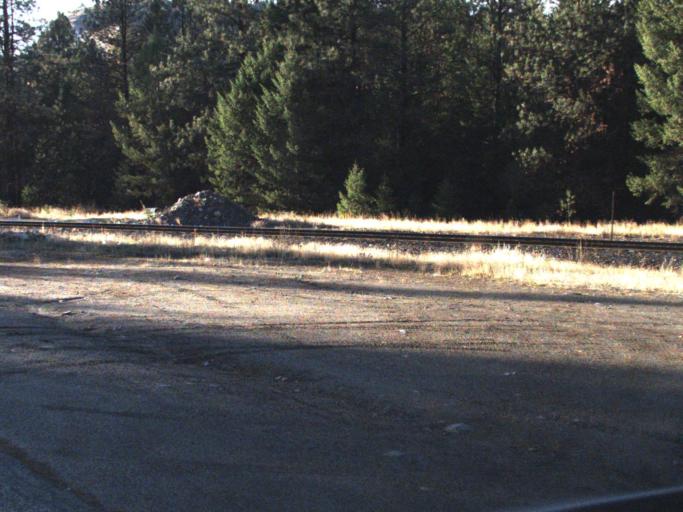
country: US
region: Washington
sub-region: Stevens County
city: Kettle Falls
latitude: 48.8139
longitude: -117.9328
